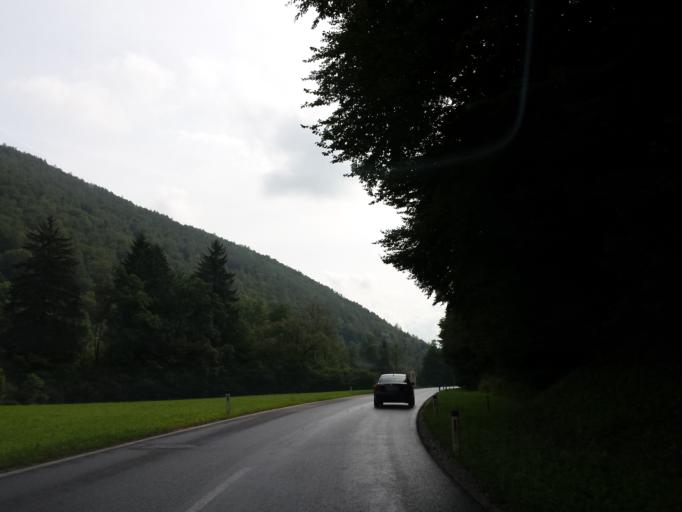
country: AT
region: Styria
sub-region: Politischer Bezirk Graz-Umgebung
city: Thal
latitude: 47.0899
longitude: 15.3737
